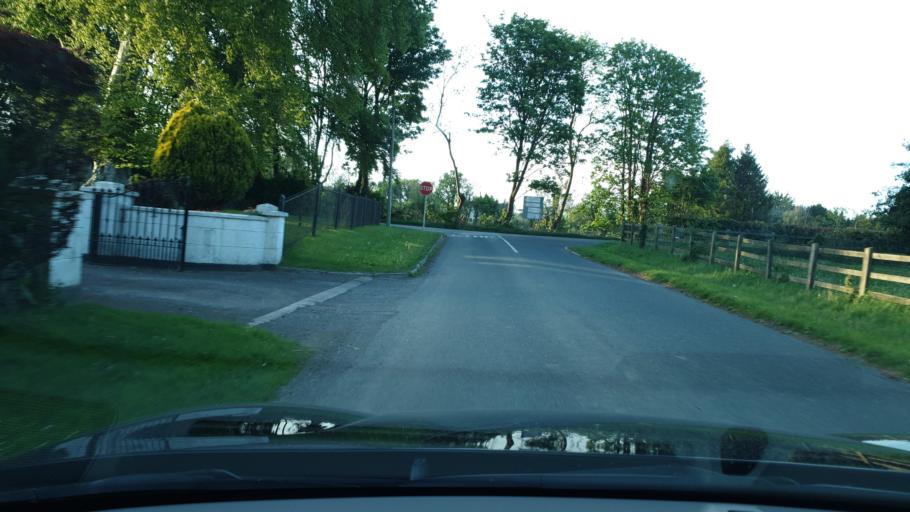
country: IE
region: Leinster
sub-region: An Mhi
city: Ashbourne
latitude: 53.4950
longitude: -6.3936
